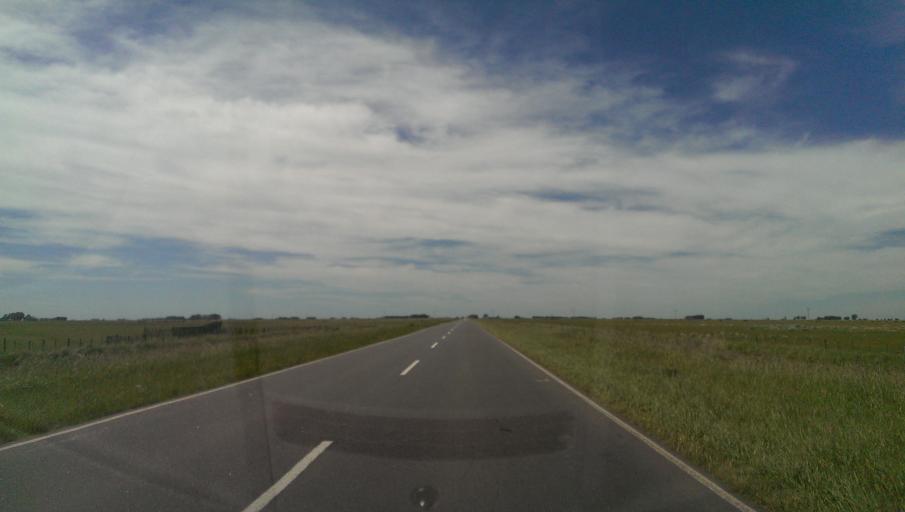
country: AR
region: Buenos Aires
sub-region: Partido de Laprida
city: Laprida
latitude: -37.2394
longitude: -60.7561
